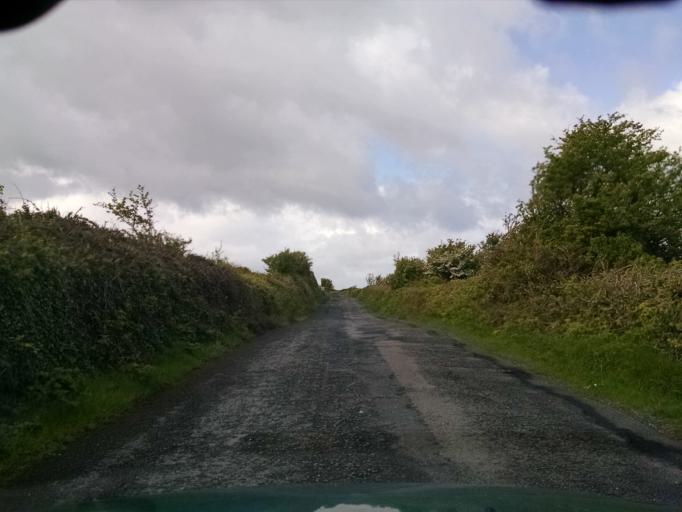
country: IE
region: Connaught
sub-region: County Galway
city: Gaillimh
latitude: 53.1562
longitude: -9.0634
